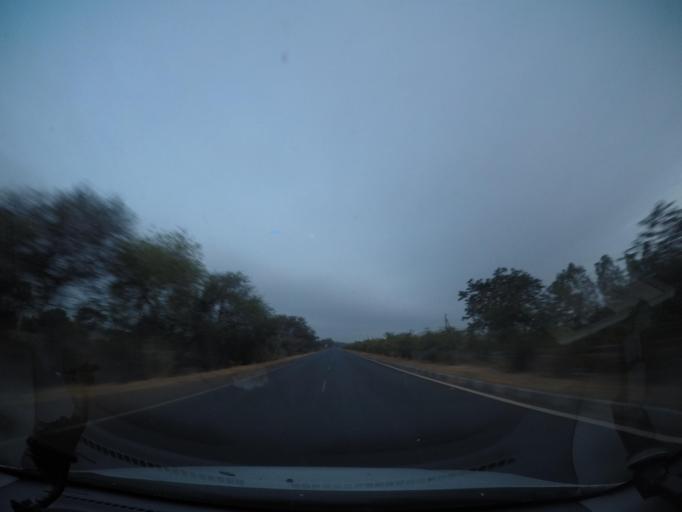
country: IN
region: Andhra Pradesh
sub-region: West Godavari
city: Tadepallegudem
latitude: 16.8145
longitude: 81.3789
